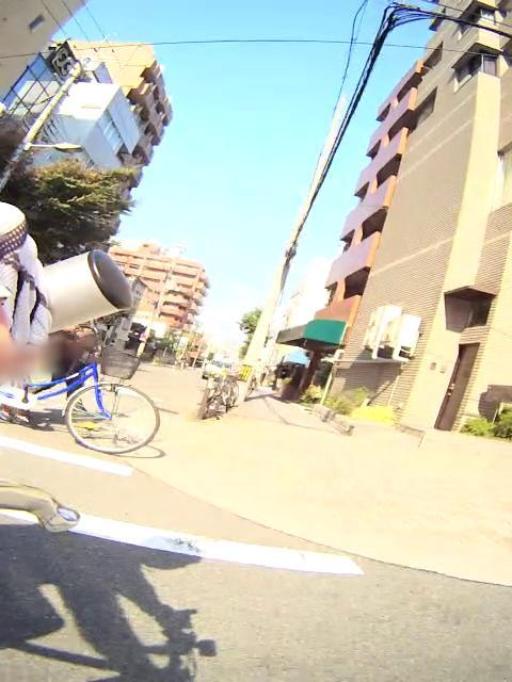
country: JP
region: Osaka
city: Suita
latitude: 34.7379
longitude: 135.4996
